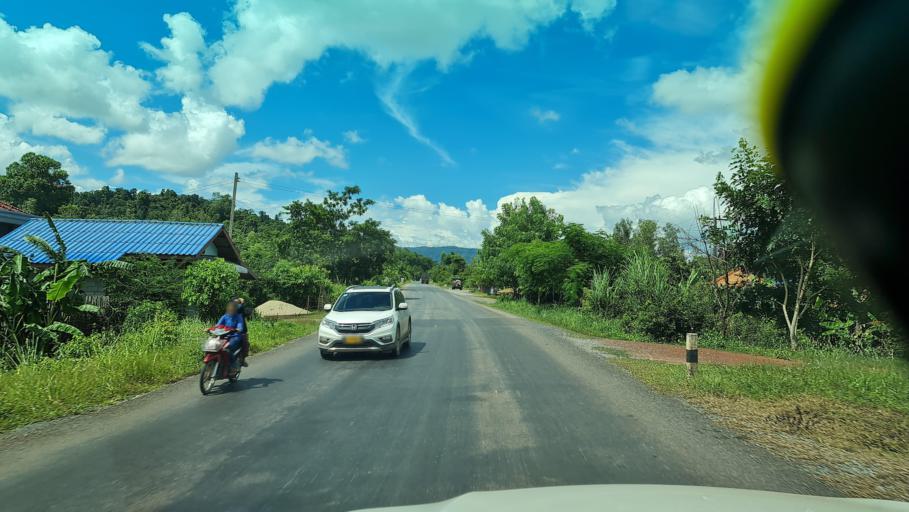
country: LA
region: Bolikhamxai
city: Pakkading
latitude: 18.2837
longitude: 104.0728
